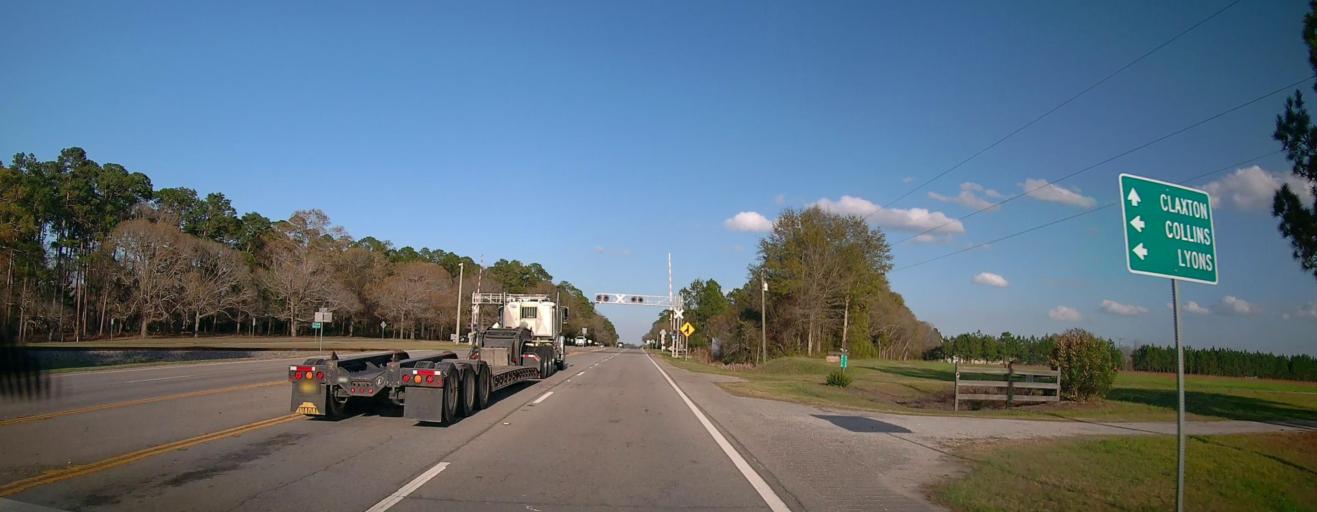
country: US
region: Georgia
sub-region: Evans County
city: Claxton
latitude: 32.1504
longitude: -81.9667
